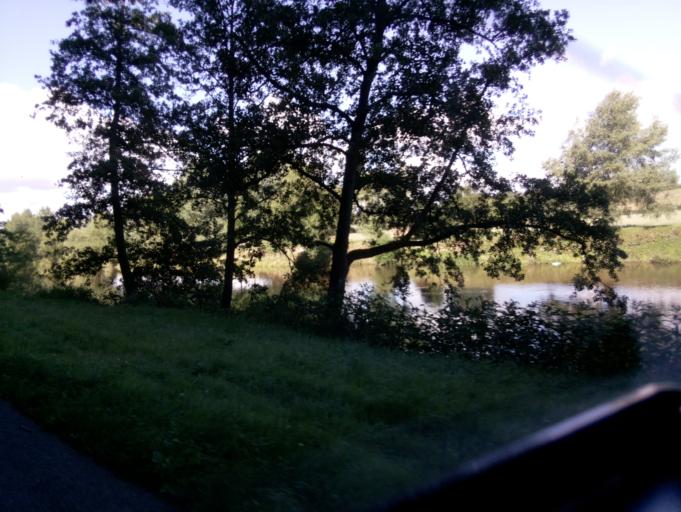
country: GB
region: England
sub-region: Herefordshire
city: Yatton
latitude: 51.9587
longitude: -2.5632
